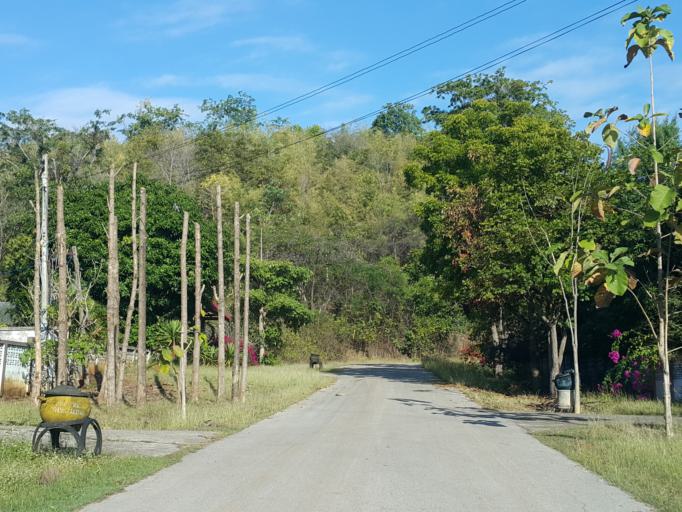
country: TH
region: Lampang
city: Mae Mo
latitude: 18.2834
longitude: 99.6434
